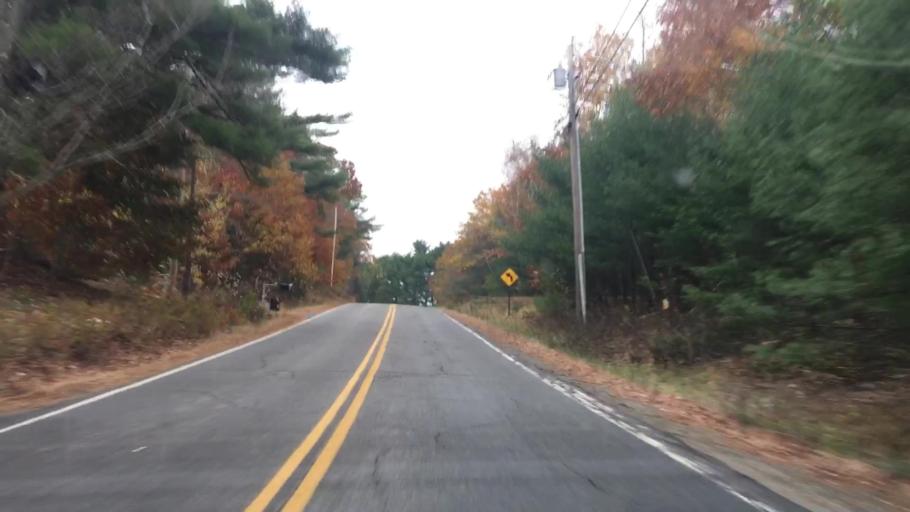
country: US
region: Maine
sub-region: Lincoln County
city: Whitefield
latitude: 44.1711
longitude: -69.6690
